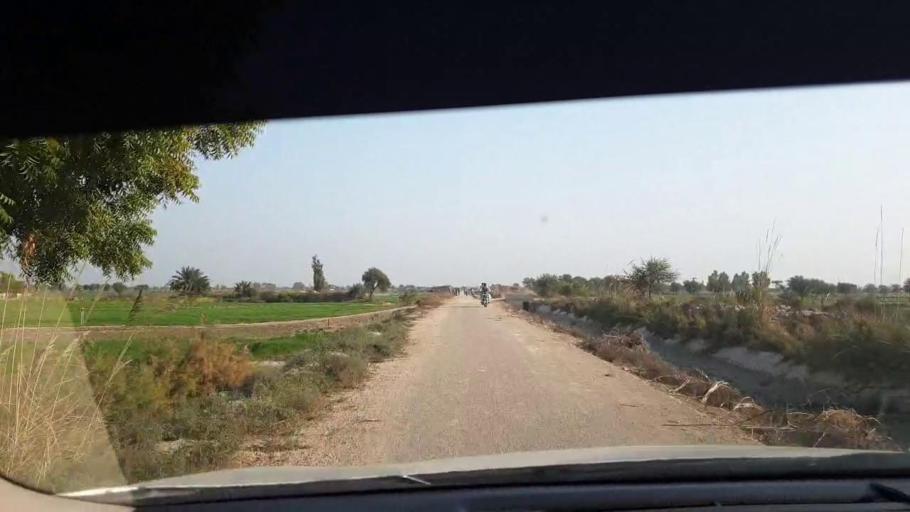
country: PK
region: Sindh
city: Berani
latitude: 25.8313
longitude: 68.7768
